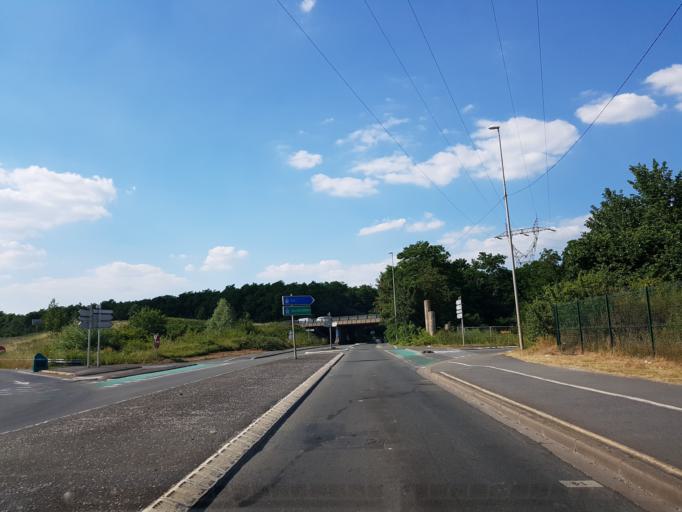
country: FR
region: Nord-Pas-de-Calais
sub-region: Departement du Nord
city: Escaudain
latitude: 50.3235
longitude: 3.3430
